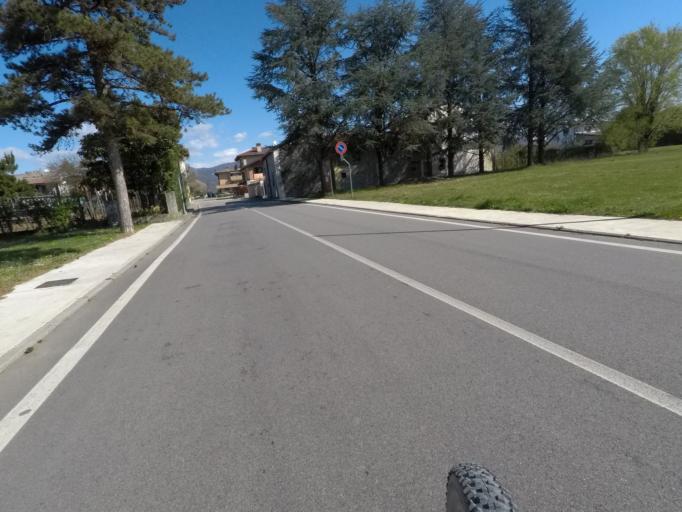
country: IT
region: Friuli Venezia Giulia
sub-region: Provincia di Udine
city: Moimacco
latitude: 46.0928
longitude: 13.3686
